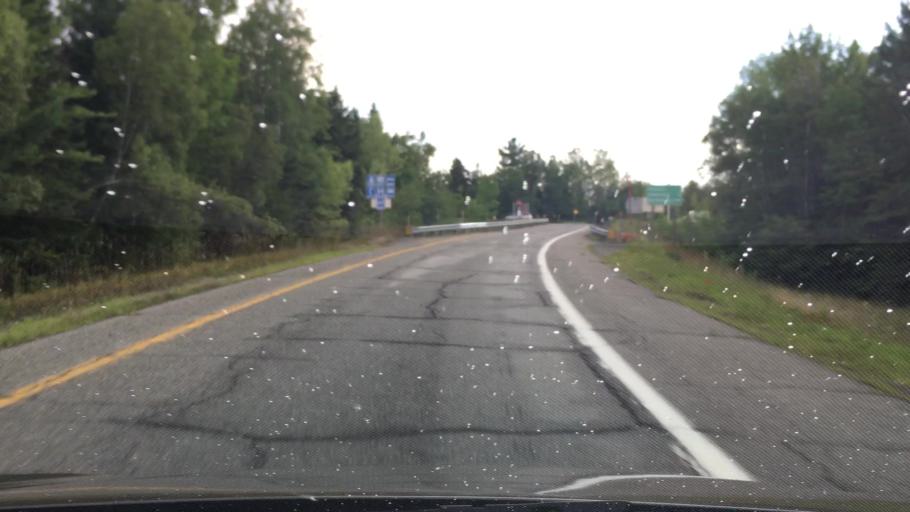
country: US
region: Maine
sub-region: Penobscot County
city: Medway
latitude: 45.6055
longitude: -68.5231
